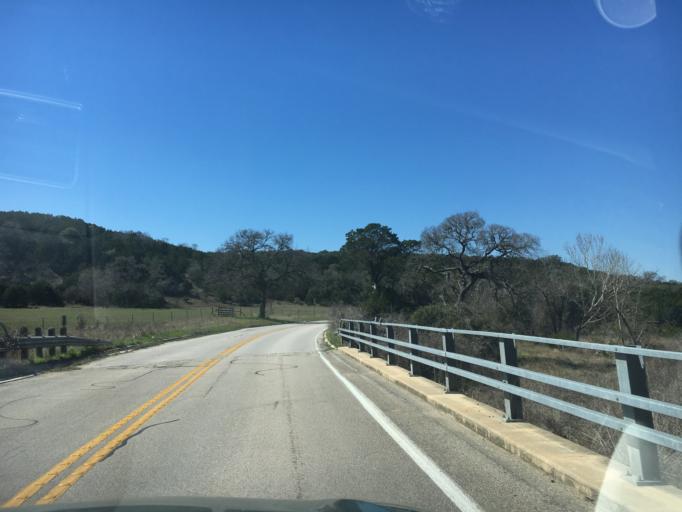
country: US
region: Texas
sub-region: Travis County
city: Briarcliff
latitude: 30.3359
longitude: -98.1272
